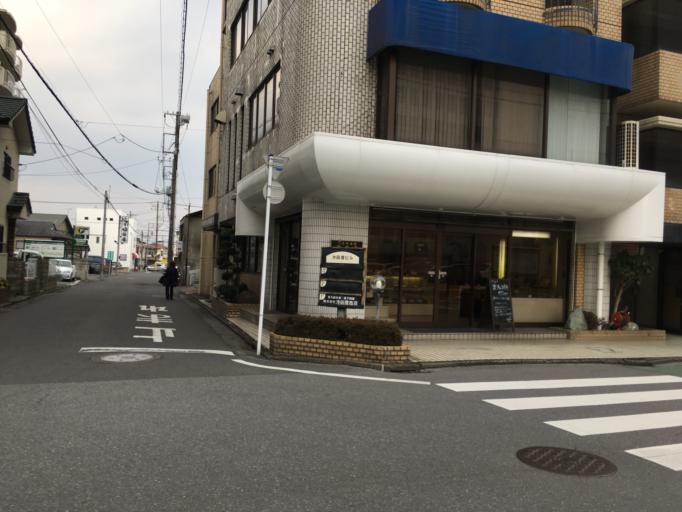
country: JP
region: Tochigi
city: Utsunomiya-shi
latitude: 36.5610
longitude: 139.8919
